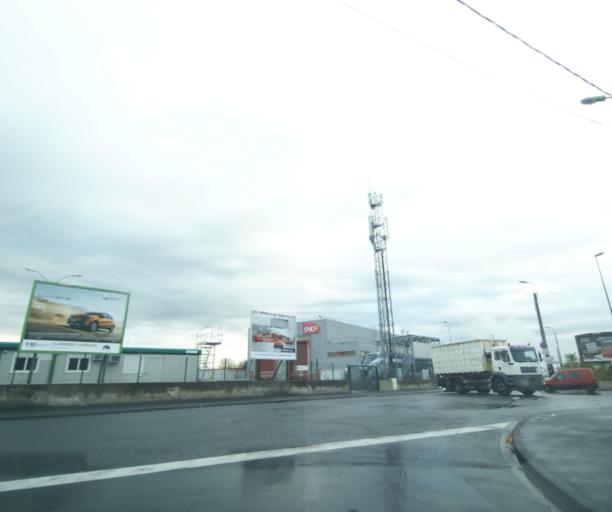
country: FR
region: Auvergne
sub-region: Departement du Puy-de-Dome
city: Aulnat
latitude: 45.7903
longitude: 3.1348
